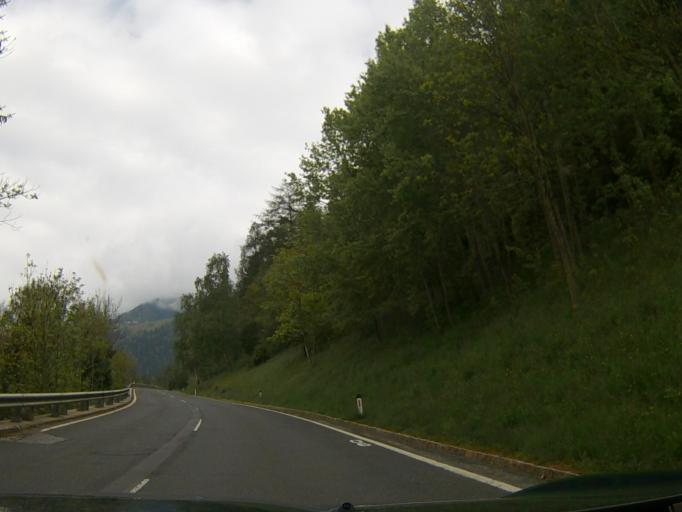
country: AT
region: Carinthia
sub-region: Politischer Bezirk Spittal an der Drau
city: Obervellach
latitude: 46.9375
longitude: 13.1971
